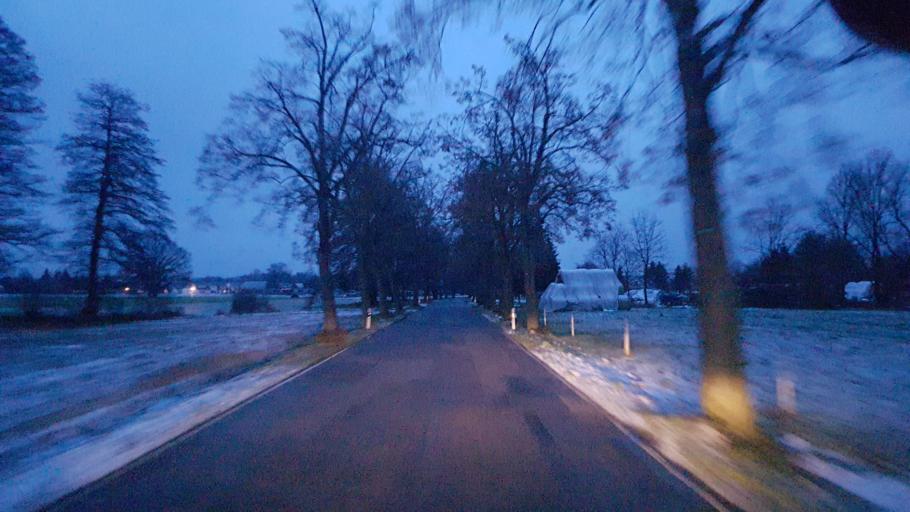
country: DE
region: Brandenburg
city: Werben
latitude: 51.7847
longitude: 14.2026
